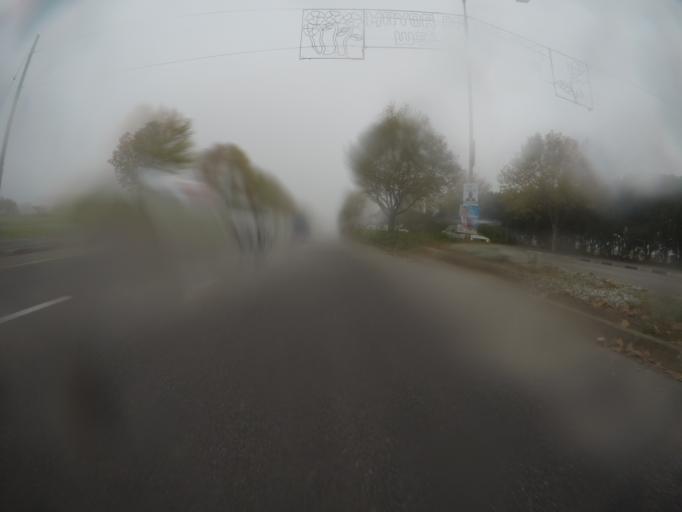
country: ZA
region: Western Cape
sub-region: Eden District Municipality
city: George
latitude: -33.9817
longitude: 22.4410
